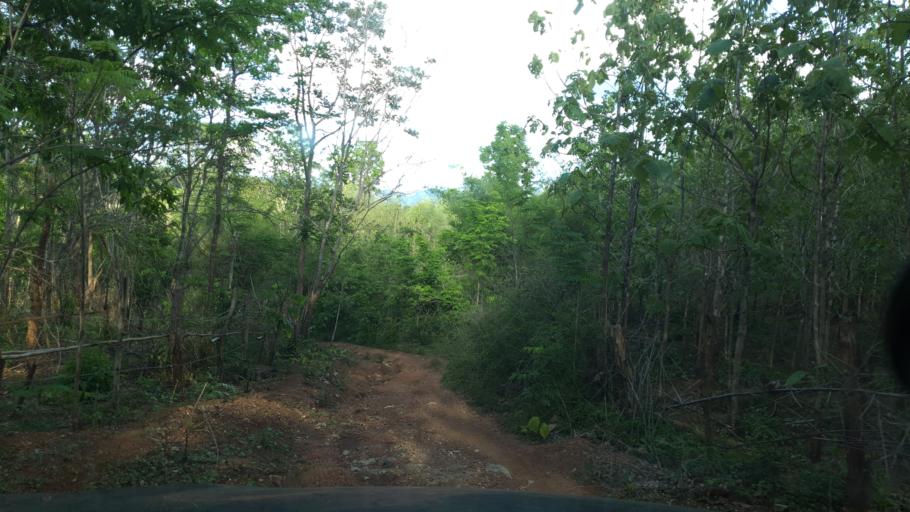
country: TH
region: Lampang
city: Sop Prap
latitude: 17.8917
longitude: 99.2852
